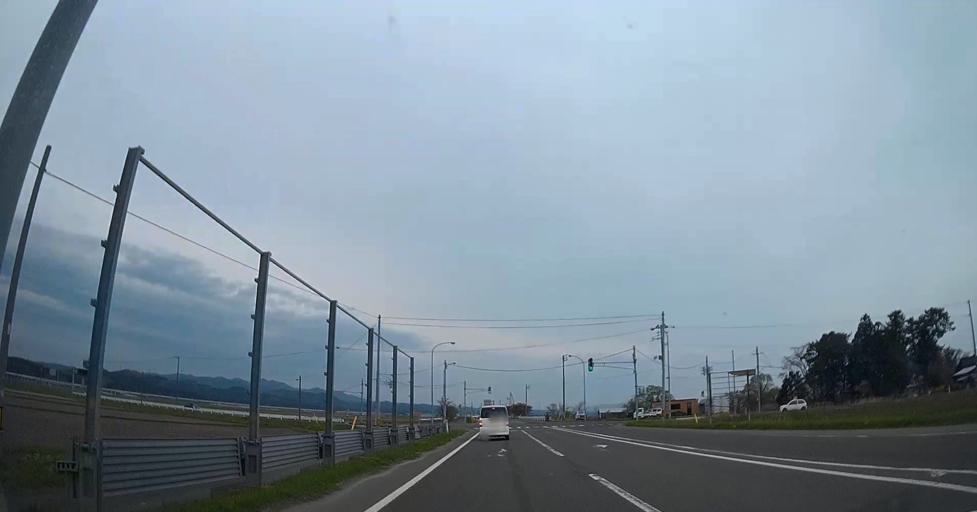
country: JP
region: Aomori
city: Aomori Shi
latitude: 40.9039
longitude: 140.6653
